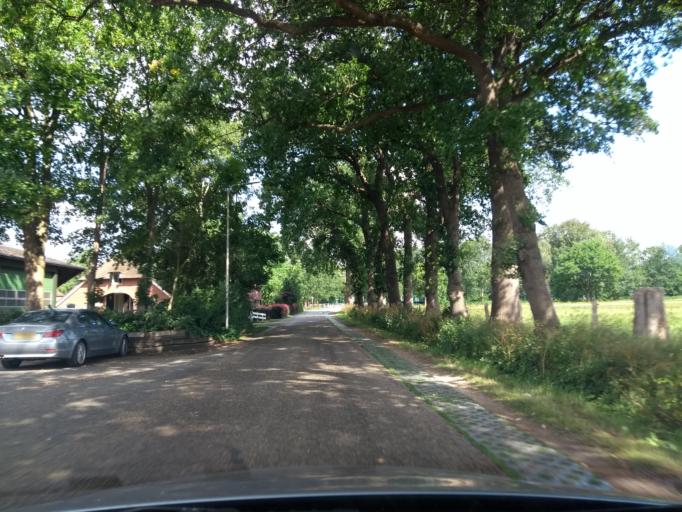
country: NL
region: Overijssel
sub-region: Gemeente Twenterand
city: Den Ham
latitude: 52.4333
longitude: 6.5059
